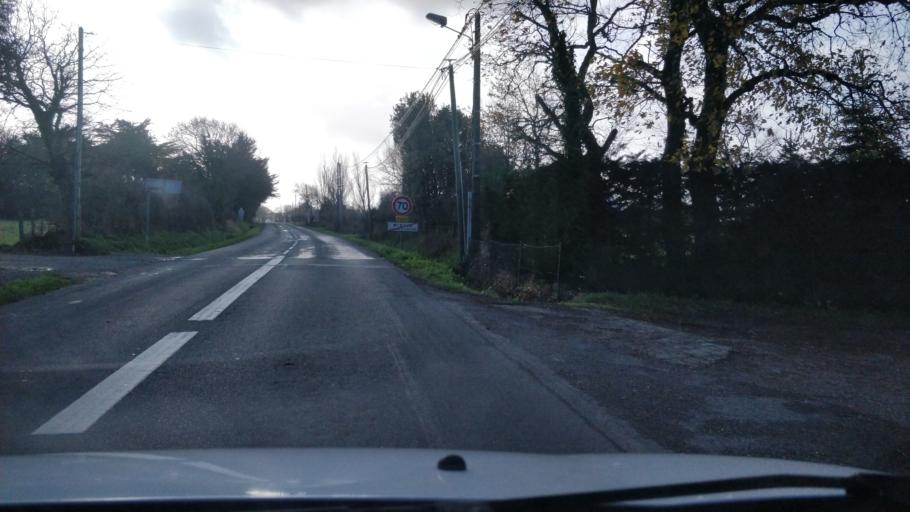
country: FR
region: Pays de la Loire
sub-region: Departement de la Loire-Atlantique
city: Guerande
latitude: 47.3521
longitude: -2.4325
